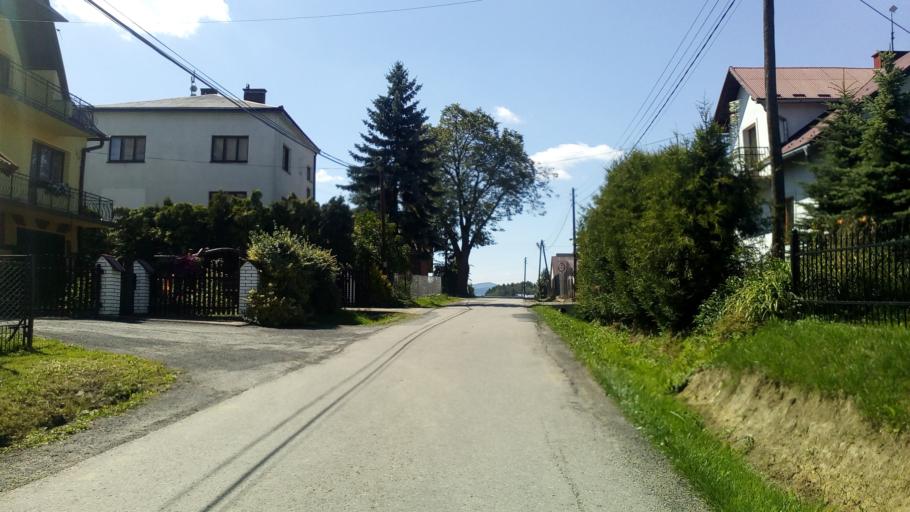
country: PL
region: Lesser Poland Voivodeship
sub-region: Powiat nowosadecki
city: Olszana
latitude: 49.5659
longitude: 20.4934
